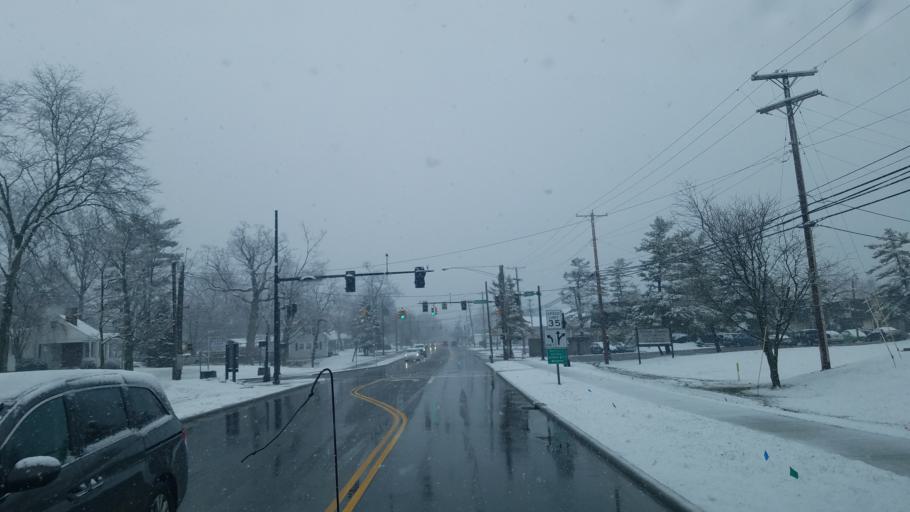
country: US
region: Ohio
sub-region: Union County
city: Marysville
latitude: 40.2390
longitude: -83.3831
